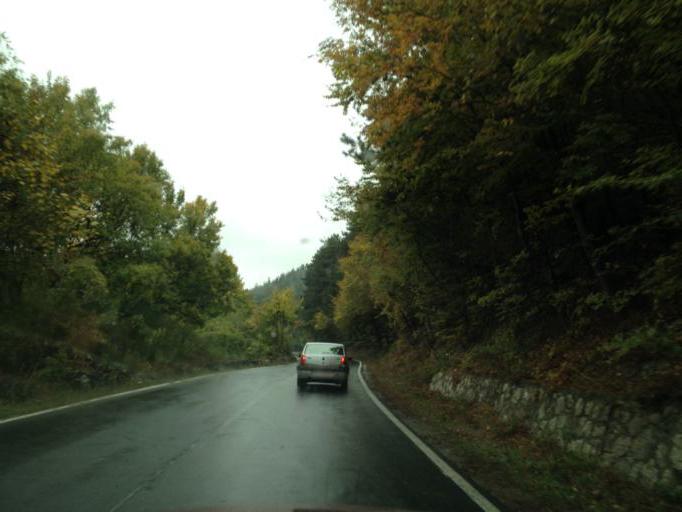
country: RO
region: Arges
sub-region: Comuna Dragoslavele
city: Dragoslavele
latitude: 45.3039
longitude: 25.1549
